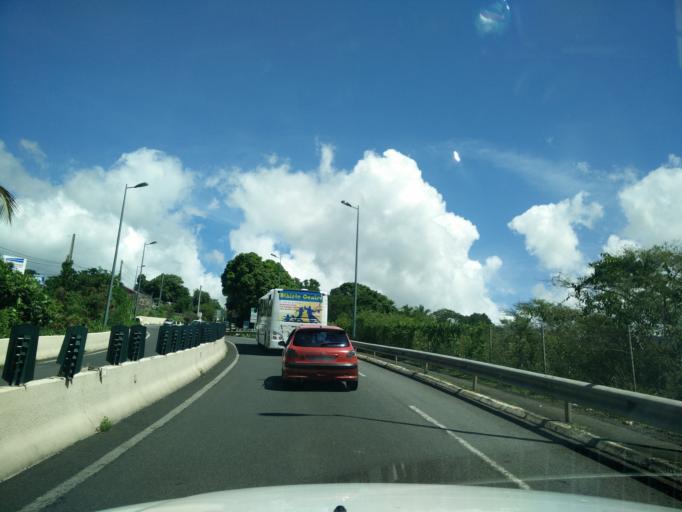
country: GP
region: Guadeloupe
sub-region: Guadeloupe
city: Basse-Terre
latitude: 15.9890
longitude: -61.7181
